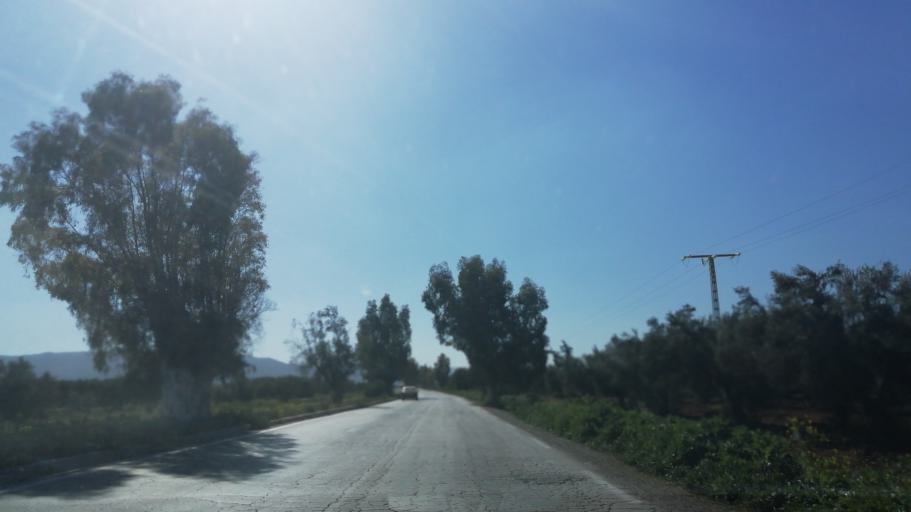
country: DZ
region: Mascara
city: Sig
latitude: 35.5556
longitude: -0.2070
